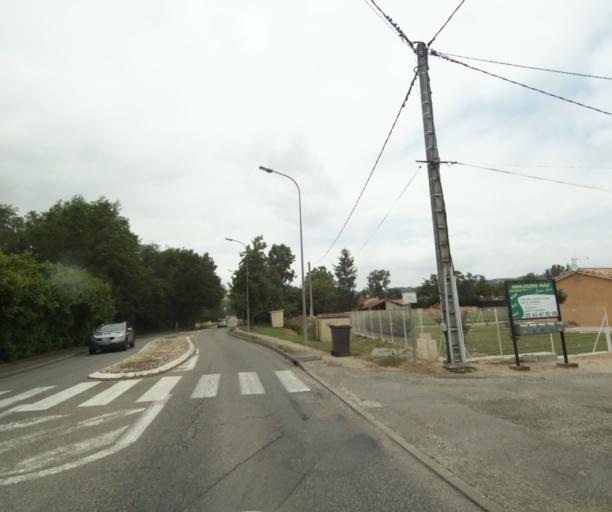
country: FR
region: Midi-Pyrenees
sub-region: Departement du Tarn-et-Garonne
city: Saint-Nauphary
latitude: 43.9696
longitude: 1.4223
